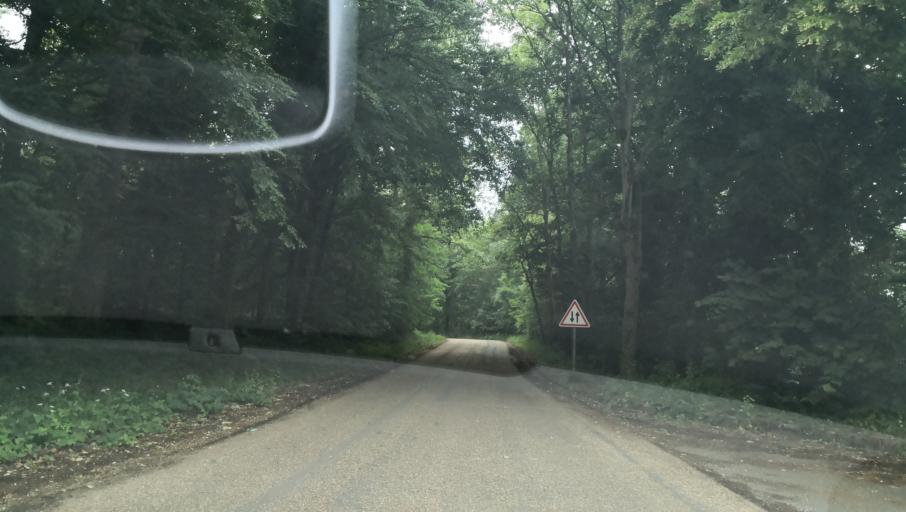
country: FR
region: Ile-de-France
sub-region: Departement des Yvelines
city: Guyancourt
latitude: 48.7810
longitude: 2.0887
